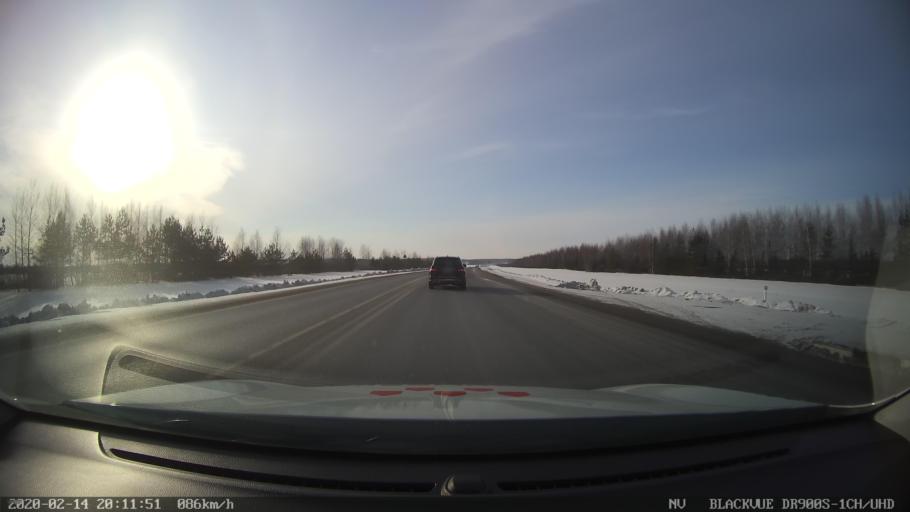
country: RU
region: Tatarstan
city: Verkhniy Uslon
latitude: 55.6726
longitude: 48.8686
